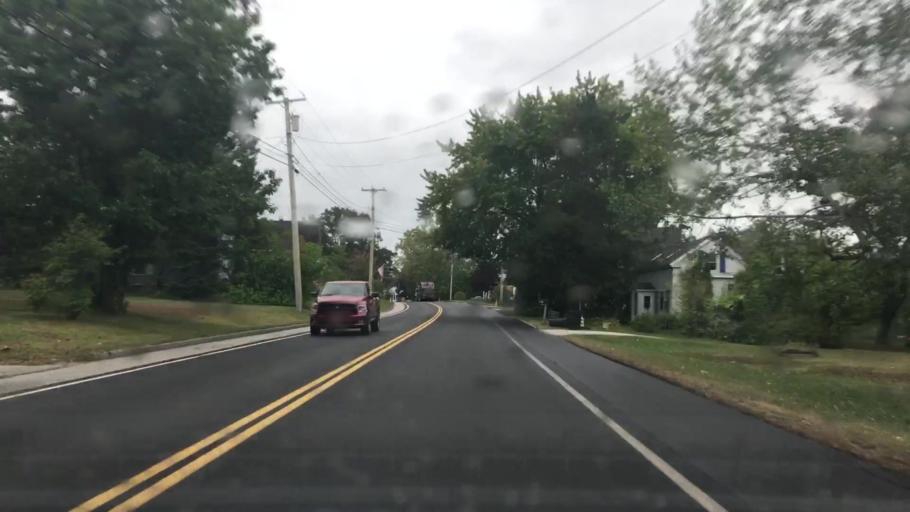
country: US
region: Maine
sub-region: Penobscot County
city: Orrington
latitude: 44.7508
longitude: -68.8042
